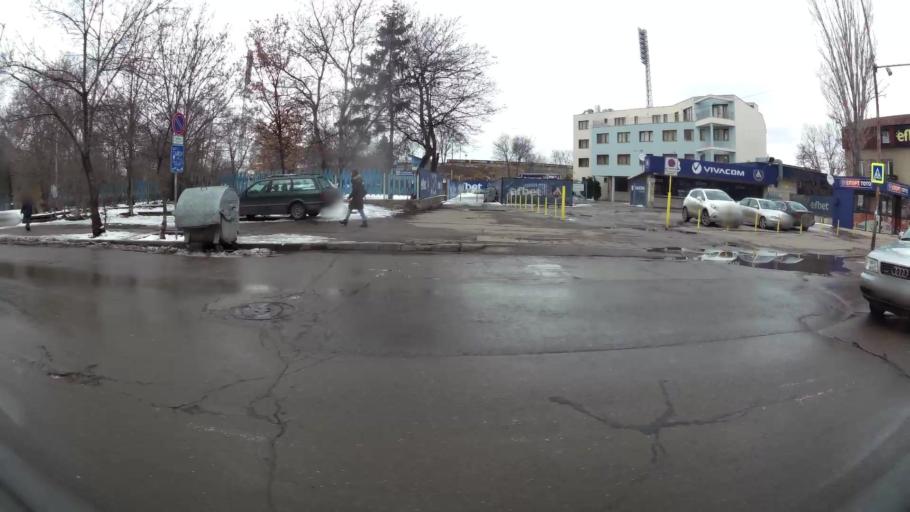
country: BG
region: Sofia-Capital
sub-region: Stolichna Obshtina
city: Sofia
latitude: 42.7035
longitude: 23.3651
